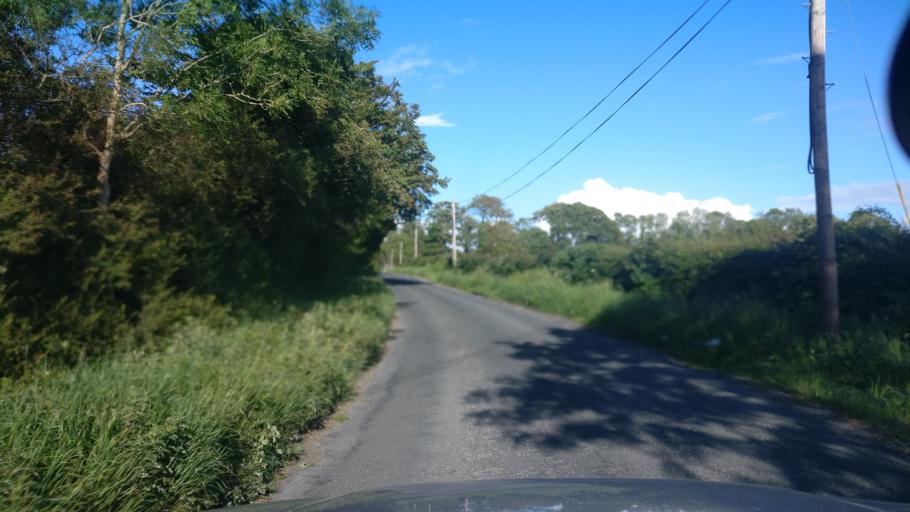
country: IE
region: Connaught
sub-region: County Galway
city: Ballinasloe
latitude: 53.2279
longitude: -8.2378
